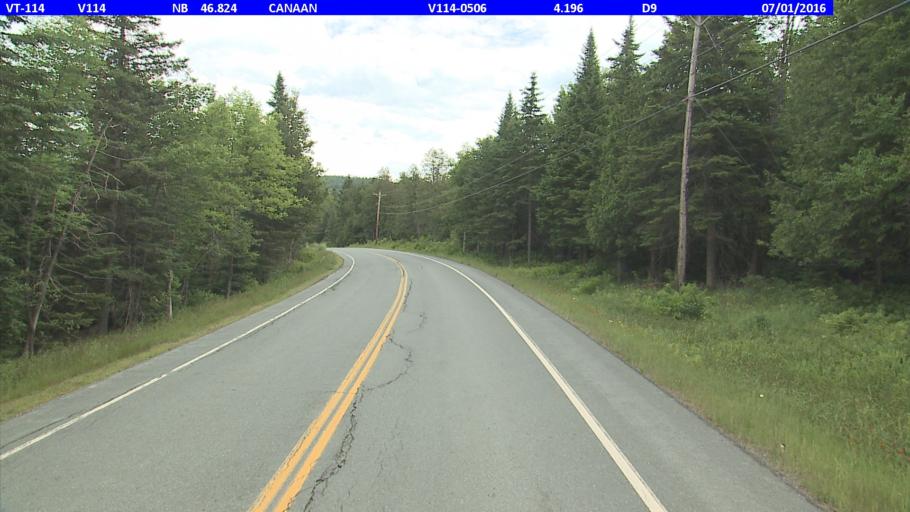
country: US
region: New Hampshire
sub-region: Coos County
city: Colebrook
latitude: 45.0080
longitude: -71.6104
